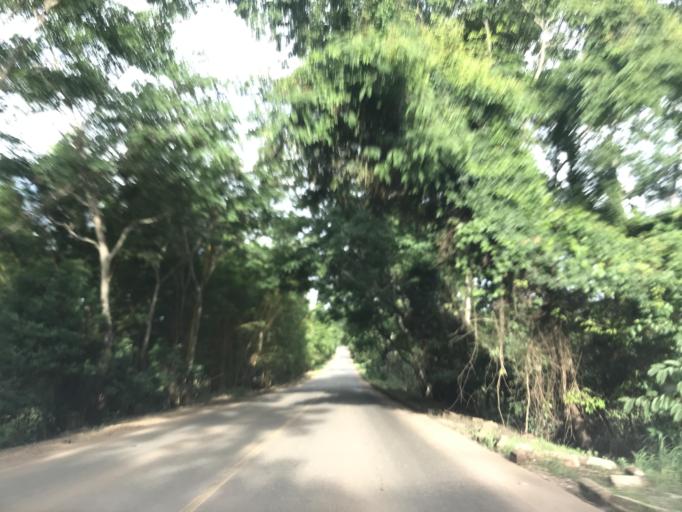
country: BR
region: Goias
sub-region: Vianopolis
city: Vianopolis
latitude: -16.5775
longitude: -48.3329
